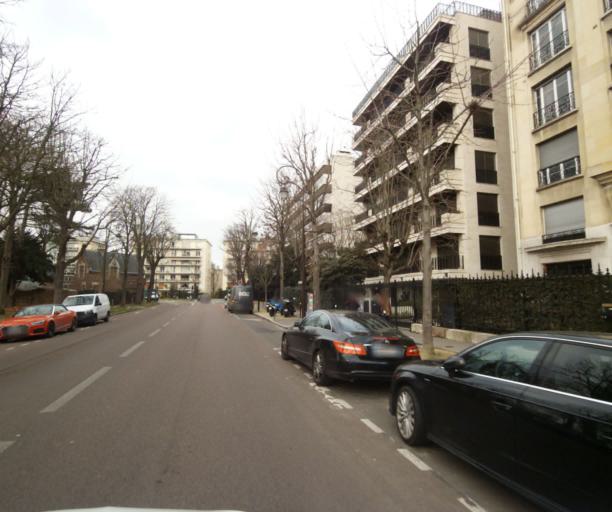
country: FR
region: Ile-de-France
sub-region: Departement des Hauts-de-Seine
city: Neuilly-sur-Seine
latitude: 48.8803
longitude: 2.2600
